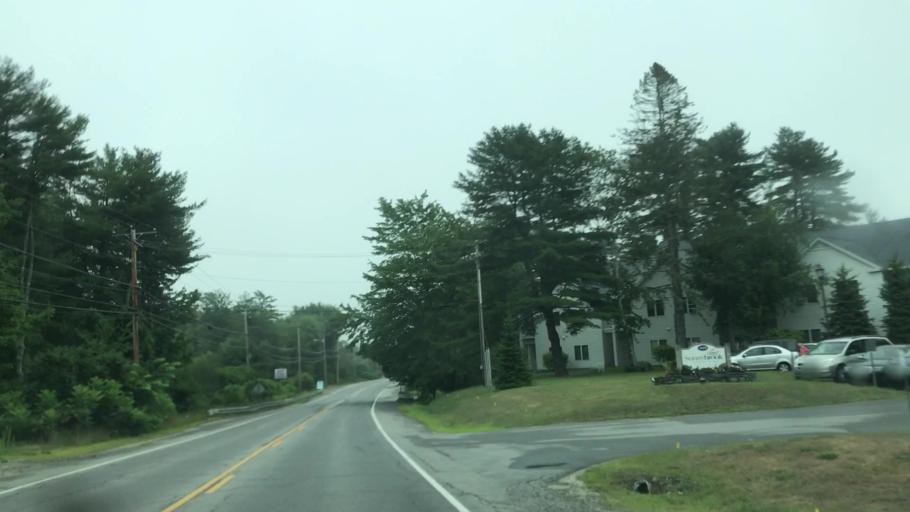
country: US
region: Maine
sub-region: Sagadahoc County
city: Bath
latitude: 43.9129
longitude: -69.8896
